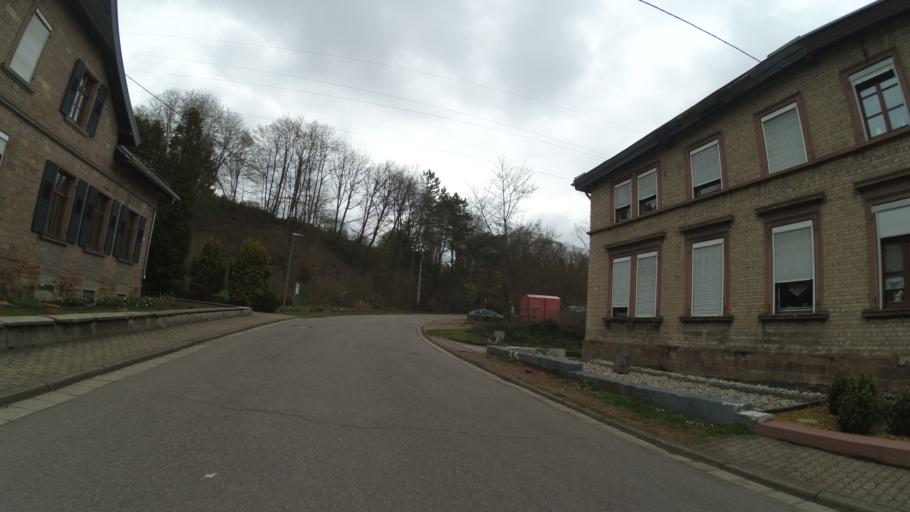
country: DE
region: Saarland
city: Quierschied
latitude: 49.3226
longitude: 7.0681
